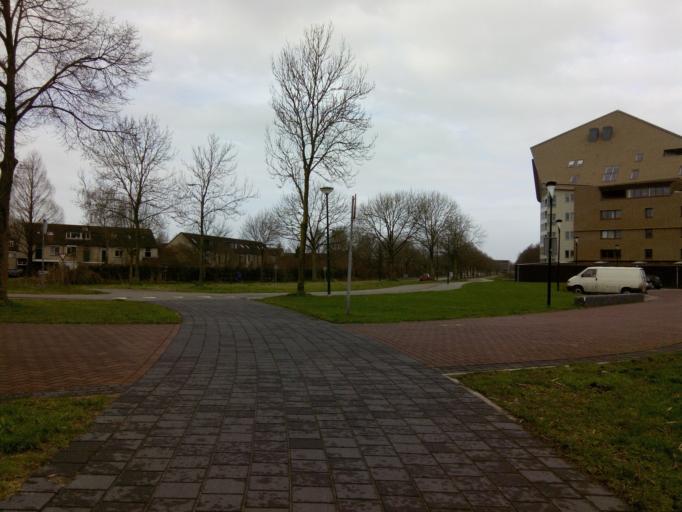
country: NL
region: Utrecht
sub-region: Gemeente Leusden
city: Leusden
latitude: 52.1411
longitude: 5.4386
